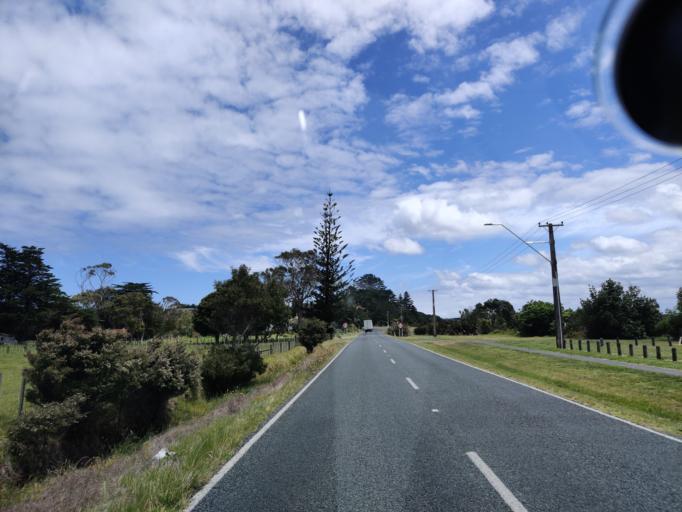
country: NZ
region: Northland
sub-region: Far North District
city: Kaitaia
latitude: -34.8192
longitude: 173.1234
